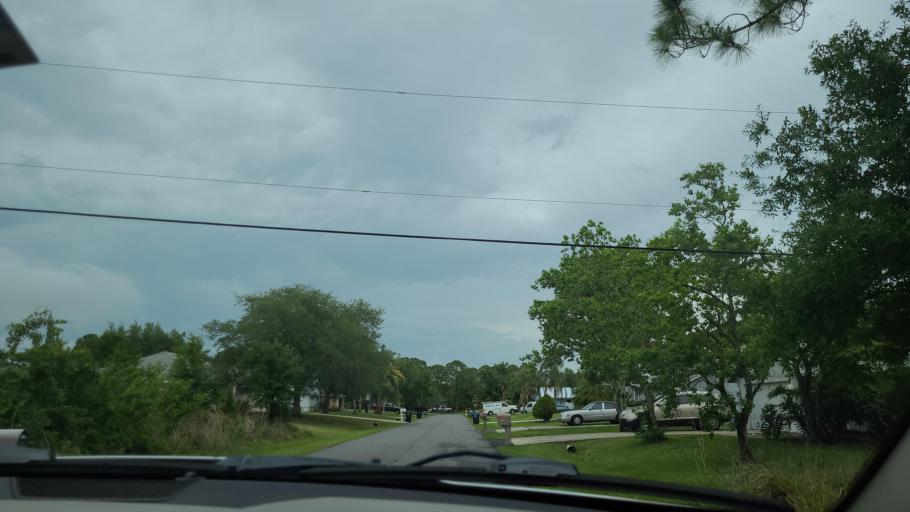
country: US
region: Florida
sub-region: Brevard County
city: Grant-Valkaria
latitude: 27.9358
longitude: -80.6294
